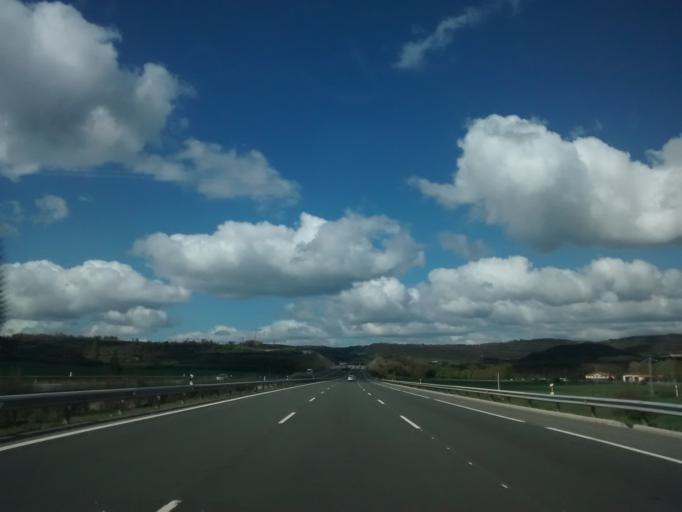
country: ES
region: Basque Country
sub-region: Provincia de Alava
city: Arminon
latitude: 42.7500
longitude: -2.8405
